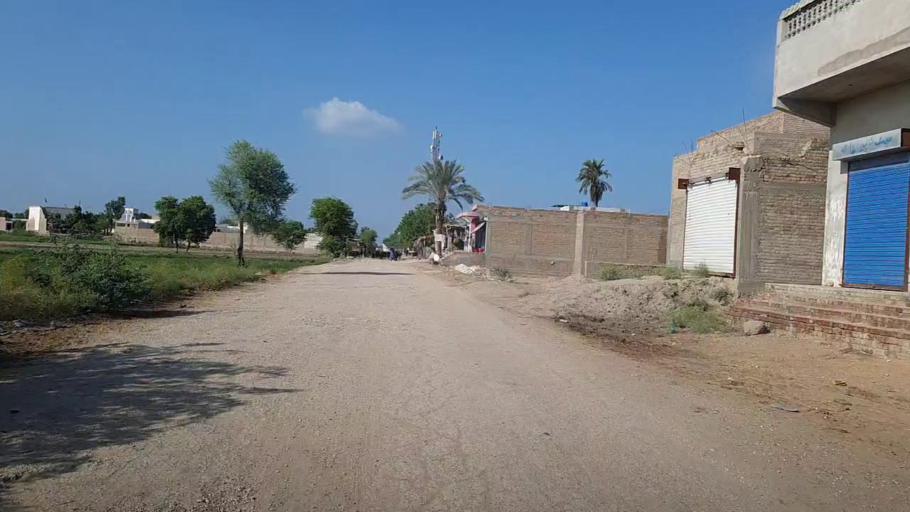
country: PK
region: Sindh
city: Kandiaro
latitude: 27.0805
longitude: 68.3160
